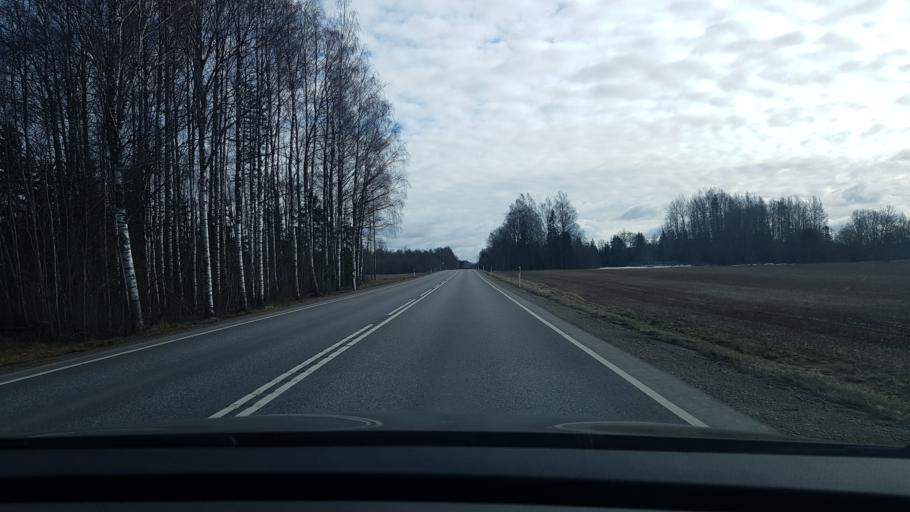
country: EE
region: Viljandimaa
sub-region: Moisakuela linn
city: Moisakula
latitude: 58.1436
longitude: 25.0893
